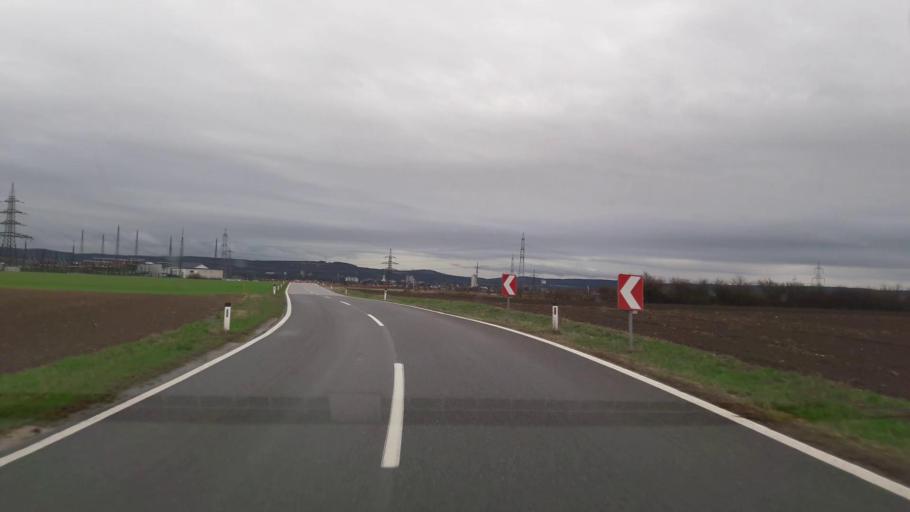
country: AT
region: Lower Austria
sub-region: Politischer Bezirk Bruck an der Leitha
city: Scharndorf
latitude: 48.0510
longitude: 16.7848
